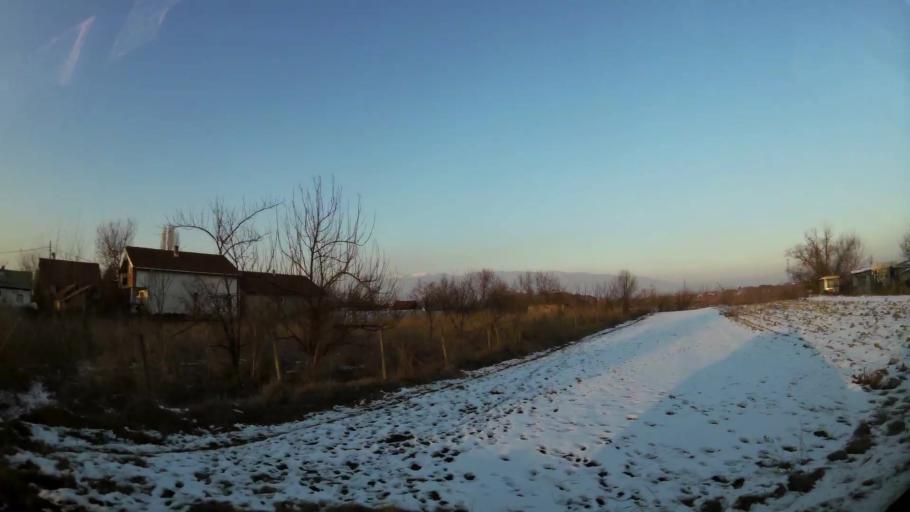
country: MK
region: Kisela Voda
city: Kisela Voda
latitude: 41.9807
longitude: 21.4935
